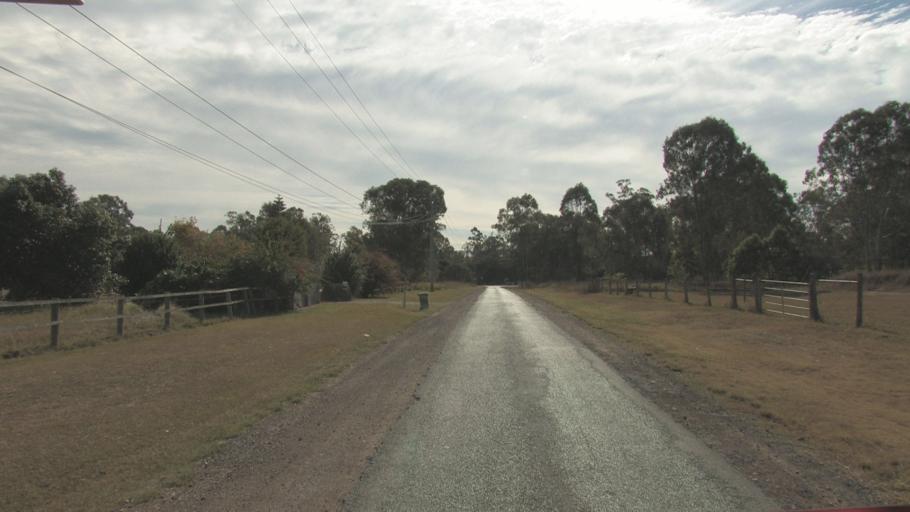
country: AU
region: Queensland
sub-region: Logan
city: North Maclean
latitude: -27.7767
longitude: 153.0083
